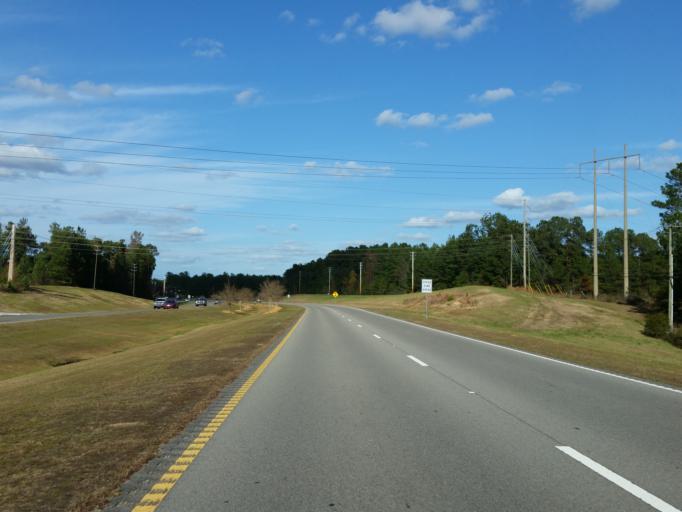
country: US
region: Mississippi
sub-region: Forrest County
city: Hattiesburg
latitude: 31.2841
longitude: -89.3239
